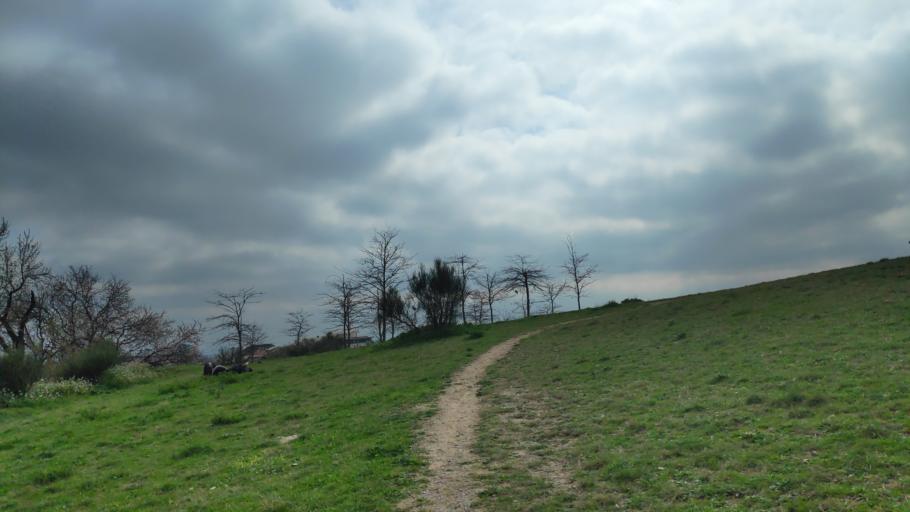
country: ES
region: Catalonia
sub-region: Provincia de Barcelona
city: Sabadell
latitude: 41.5527
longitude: 2.0948
